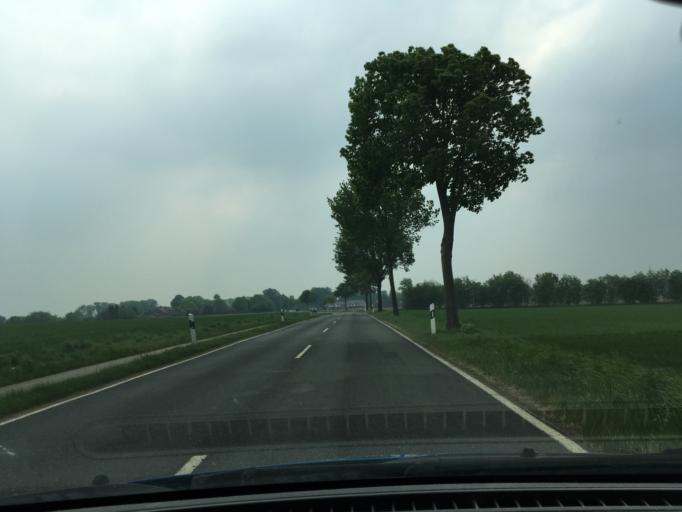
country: DE
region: Lower Saxony
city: Buchholz in der Nordheide
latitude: 53.3890
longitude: 9.8600
